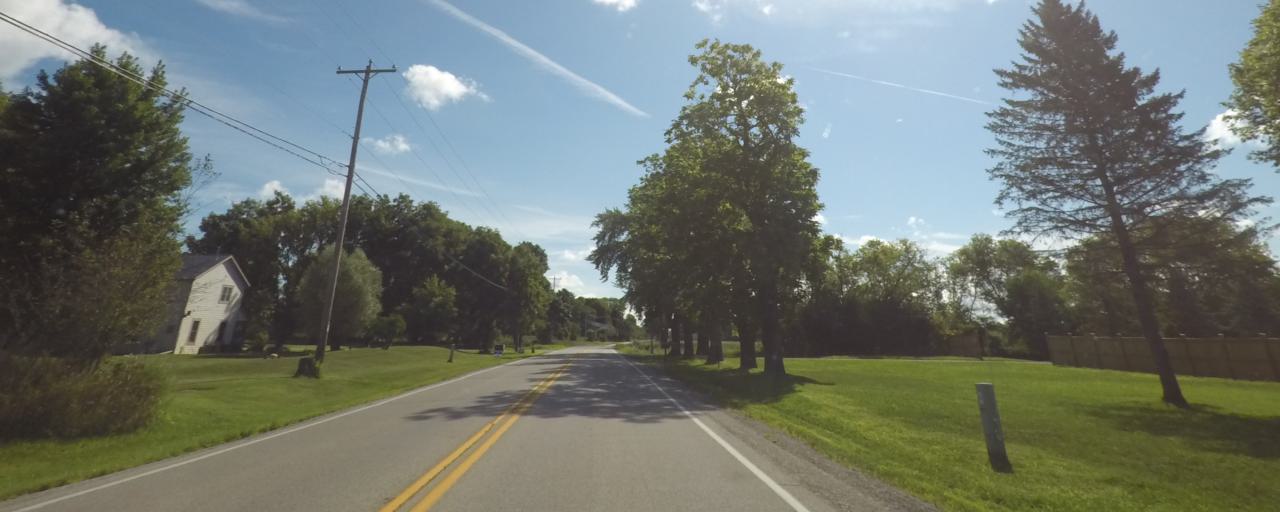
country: US
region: Wisconsin
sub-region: Waukesha County
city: Oconomowoc
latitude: 43.0839
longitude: -88.5271
